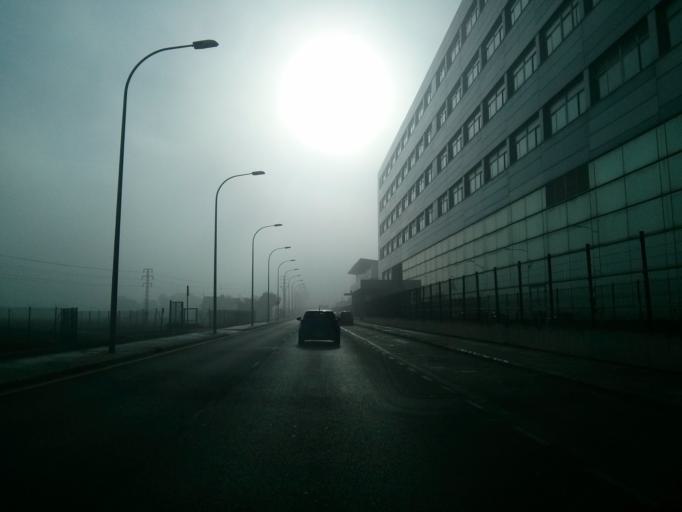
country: ES
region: Valencia
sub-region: Provincia de Valencia
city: Alboraya
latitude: 39.4847
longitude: -0.3439
